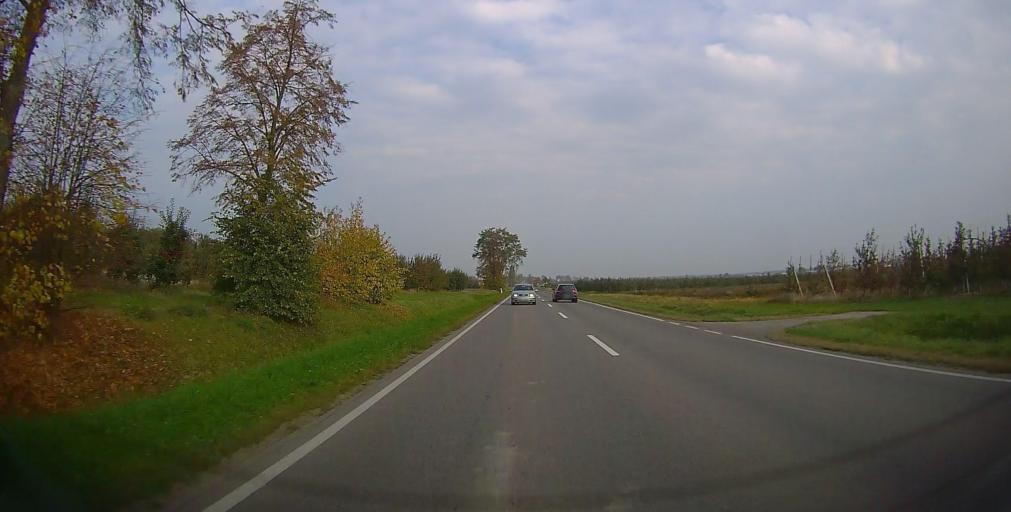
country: PL
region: Masovian Voivodeship
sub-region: Powiat grojecki
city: Bledow
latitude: 51.7606
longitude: 20.7666
